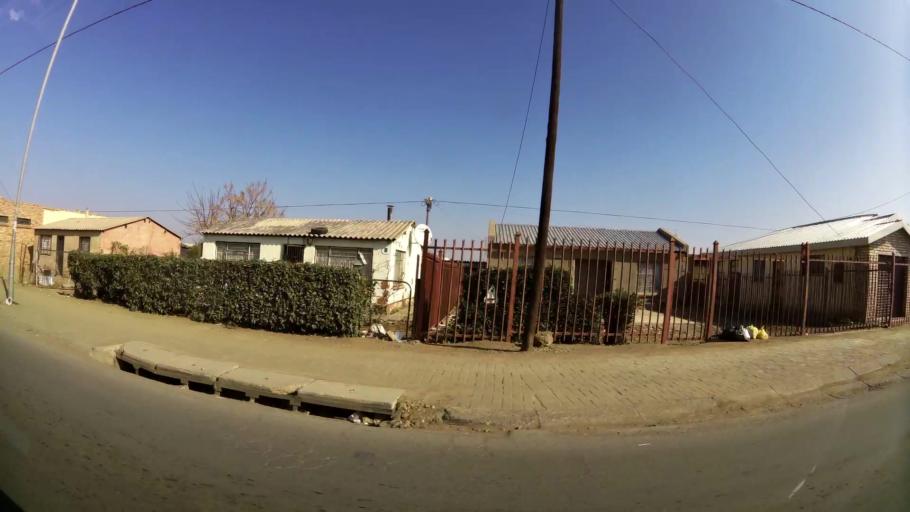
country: ZA
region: Orange Free State
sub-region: Mangaung Metropolitan Municipality
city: Bloemfontein
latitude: -29.1669
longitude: 26.2367
